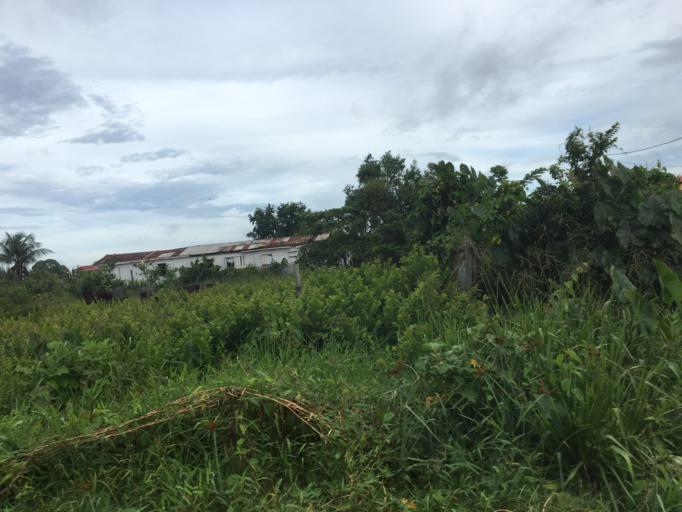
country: GY
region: Demerara-Mahaica
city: Georgetown
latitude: 6.7970
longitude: -58.1218
